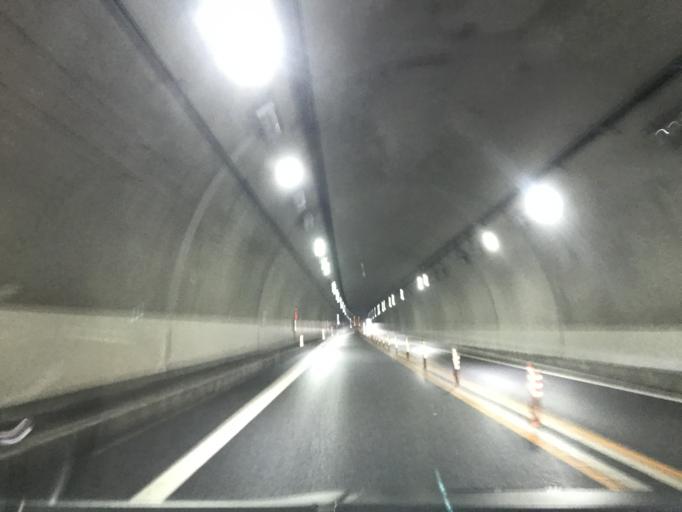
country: JP
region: Fukuoka
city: Nakatsu
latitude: 33.5116
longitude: 131.2850
